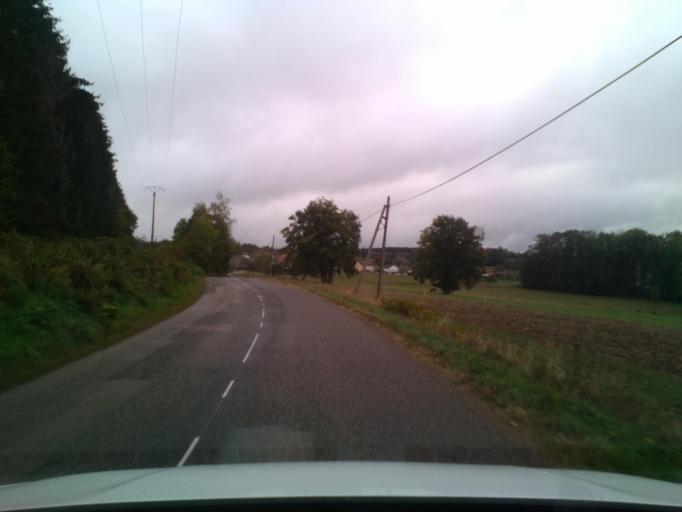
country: FR
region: Lorraine
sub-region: Departement des Vosges
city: Senones
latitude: 48.3698
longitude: 6.9502
